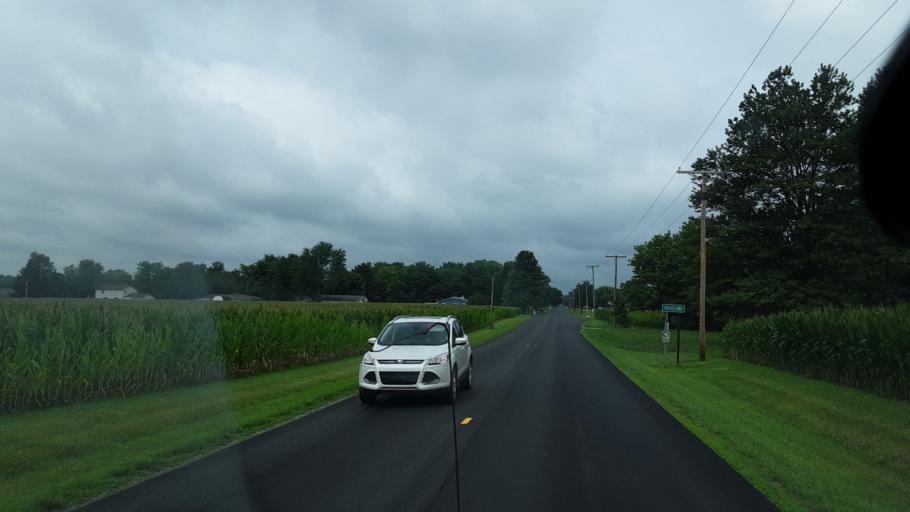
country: US
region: Indiana
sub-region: Allen County
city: Monroeville
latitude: 40.9484
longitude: -84.9781
